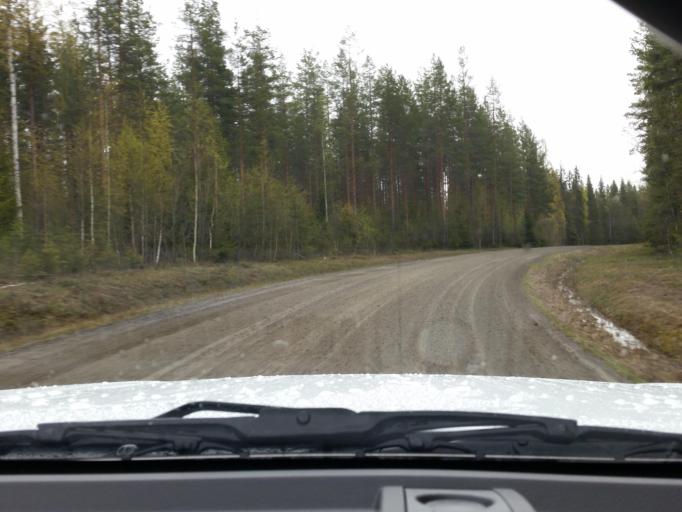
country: SE
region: Norrbotten
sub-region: Pitea Kommun
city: Norrfjarden
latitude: 65.5917
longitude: 21.4563
